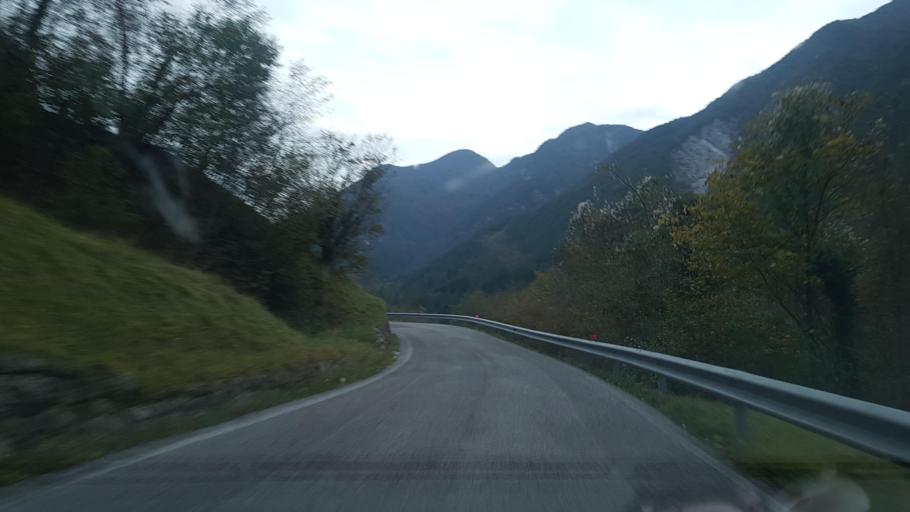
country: IT
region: Friuli Venezia Giulia
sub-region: Provincia di Udine
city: Chiaulis
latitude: 46.3221
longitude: 12.9409
